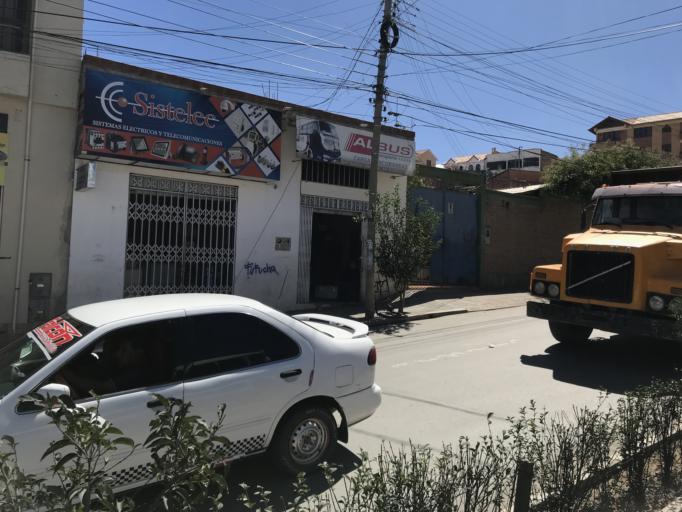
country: BO
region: Chuquisaca
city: Sucre
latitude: -19.0382
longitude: -65.2448
